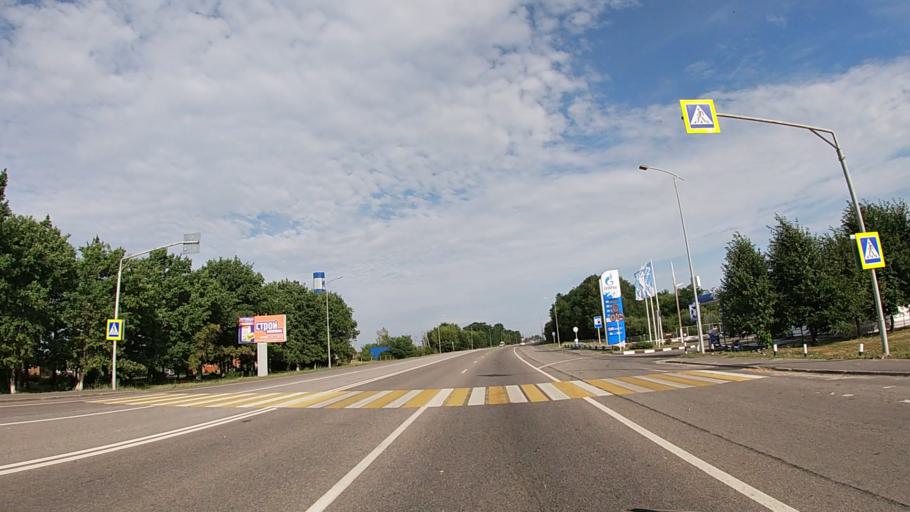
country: RU
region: Belgorod
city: Severnyy
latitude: 50.6384
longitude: 36.4437
